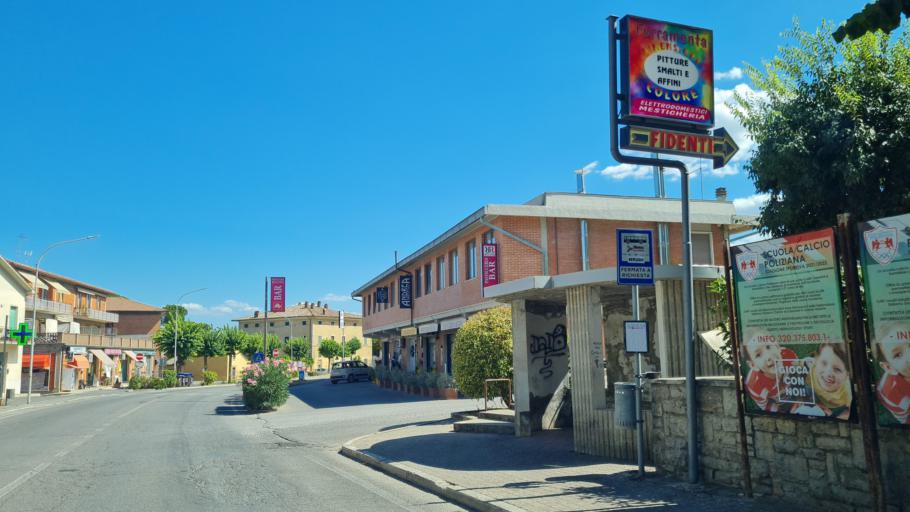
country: IT
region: Tuscany
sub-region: Provincia di Siena
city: Sant'Albino
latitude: 43.0714
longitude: 11.8059
